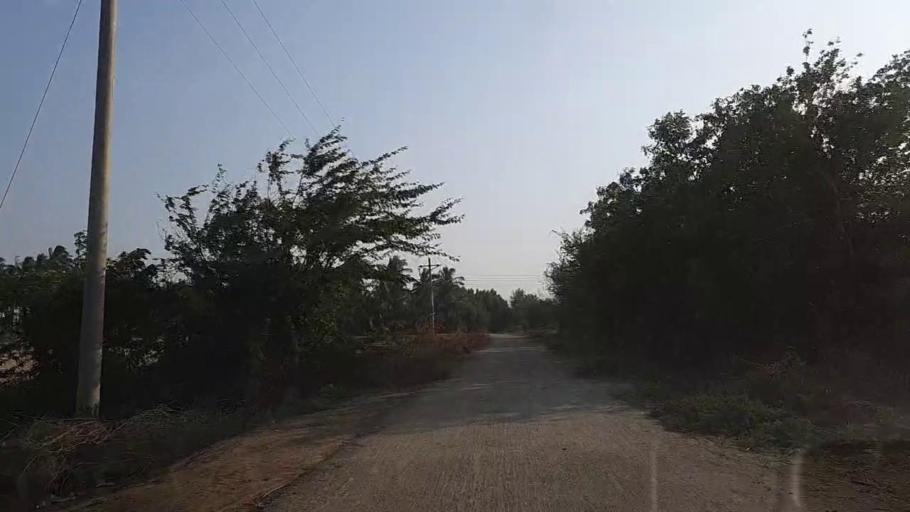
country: PK
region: Sindh
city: Keti Bandar
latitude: 24.1650
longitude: 67.6279
